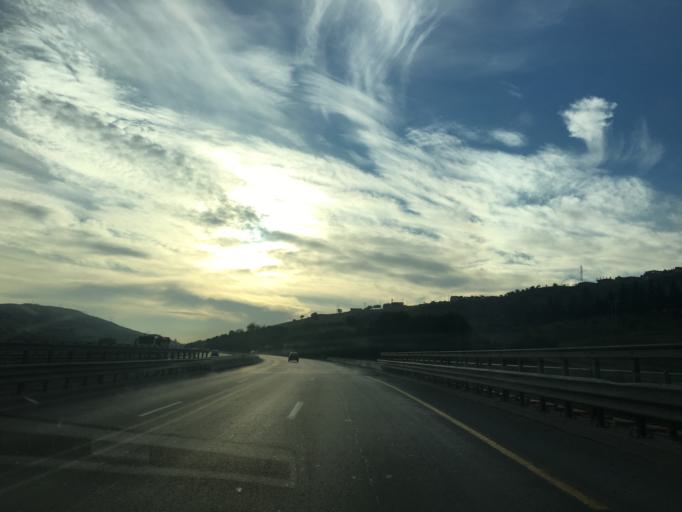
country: DZ
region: Bouira
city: Draa el Mizan
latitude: 36.4615
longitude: 3.7708
